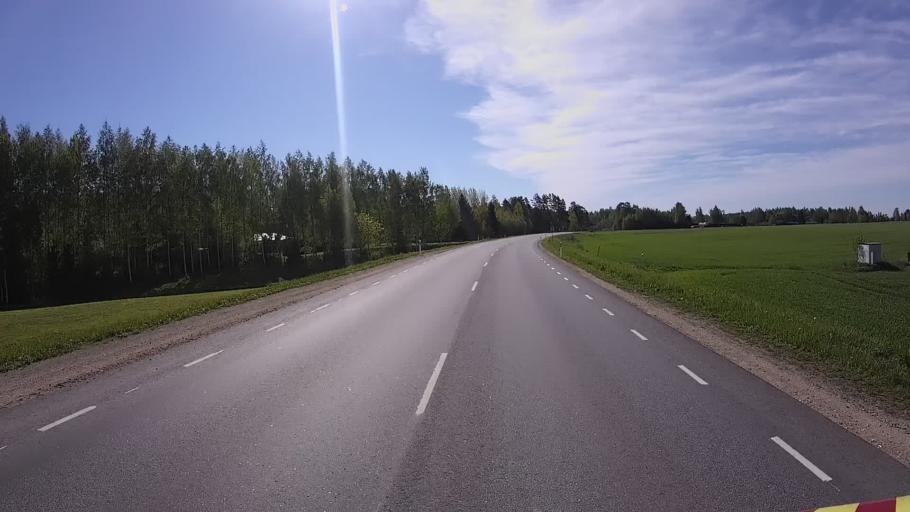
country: EE
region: Tartu
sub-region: UElenurme vald
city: Ulenurme
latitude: 58.3367
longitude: 26.9717
